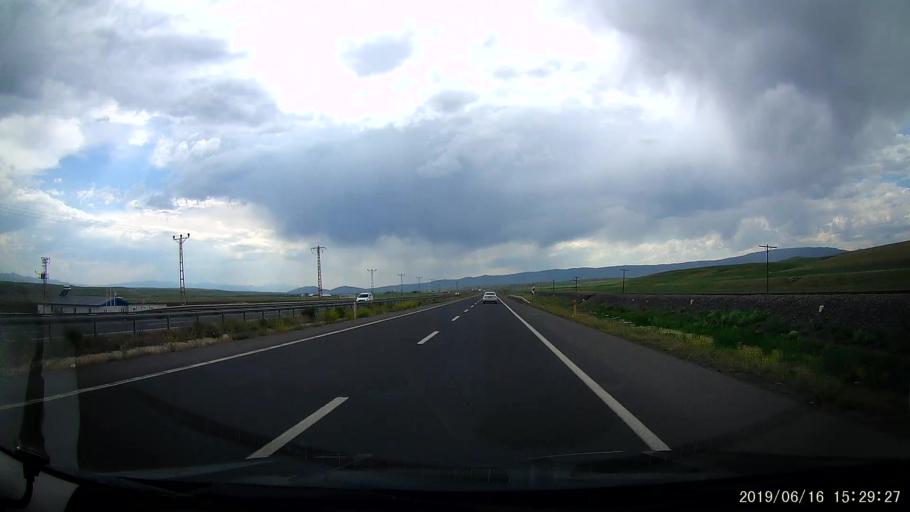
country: TR
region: Erzurum
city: Horasan
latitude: 40.0317
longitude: 42.1315
